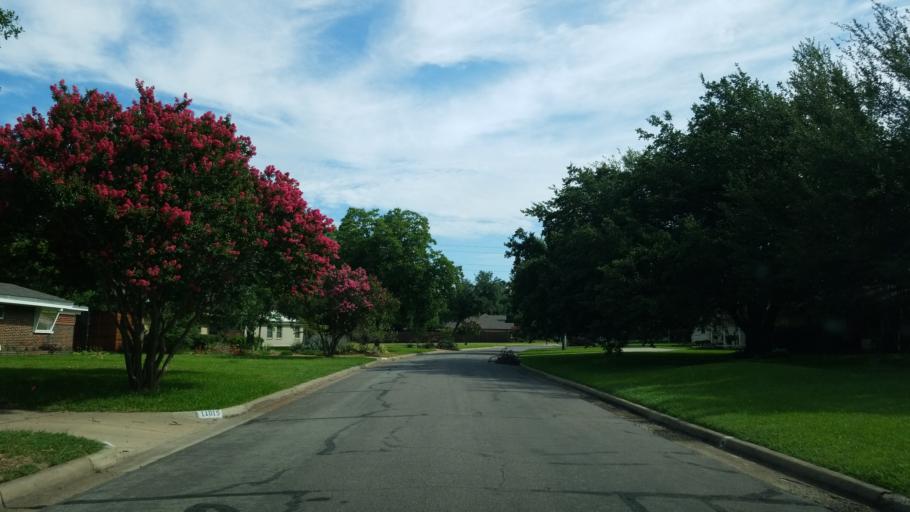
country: US
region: Texas
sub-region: Dallas County
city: Farmers Branch
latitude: 32.8985
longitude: -96.8413
